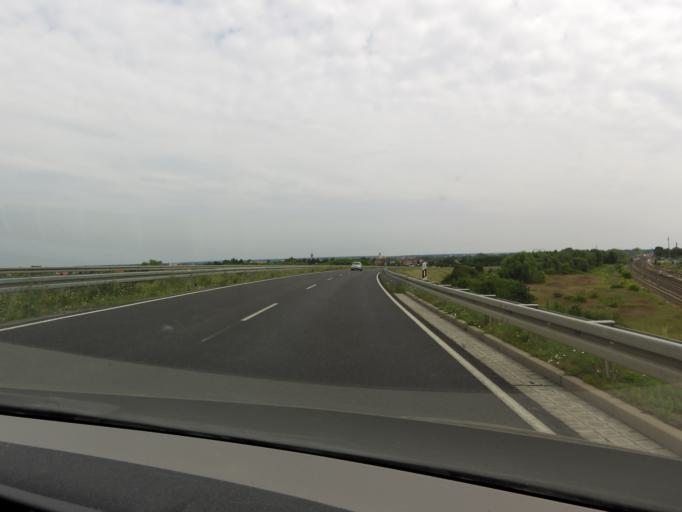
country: DE
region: Saxony-Anhalt
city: Wittenburg
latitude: 51.8388
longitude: 12.6276
